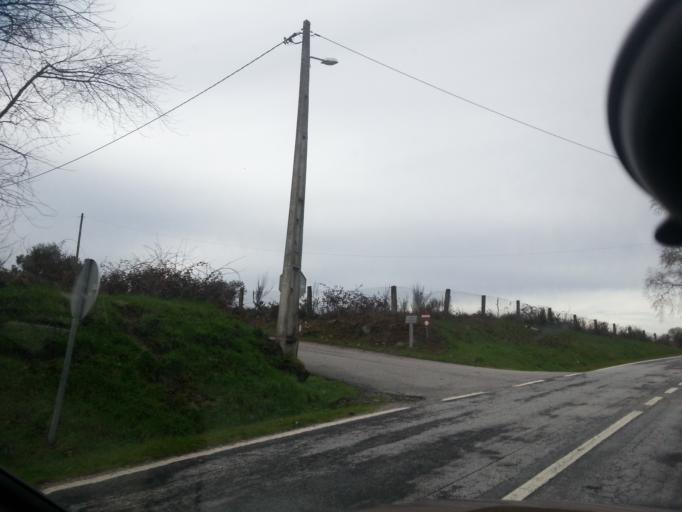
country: PT
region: Guarda
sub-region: Fornos de Algodres
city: Fornos de Algodres
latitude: 40.5291
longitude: -7.5808
